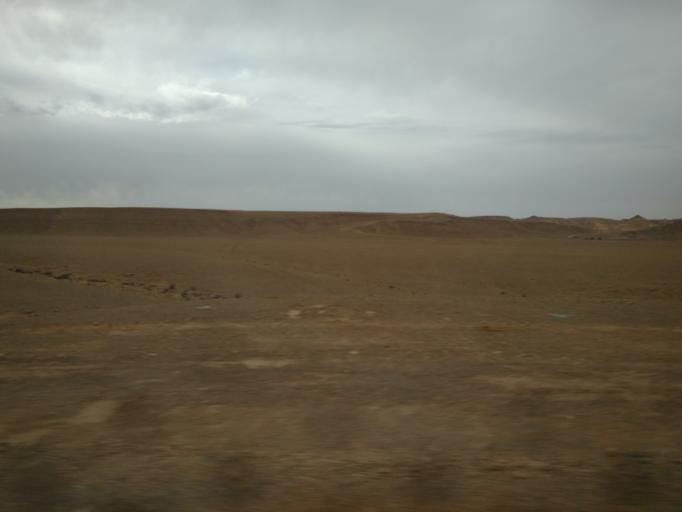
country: IL
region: Southern District
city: Eilat
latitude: 29.8554
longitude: 34.8435
